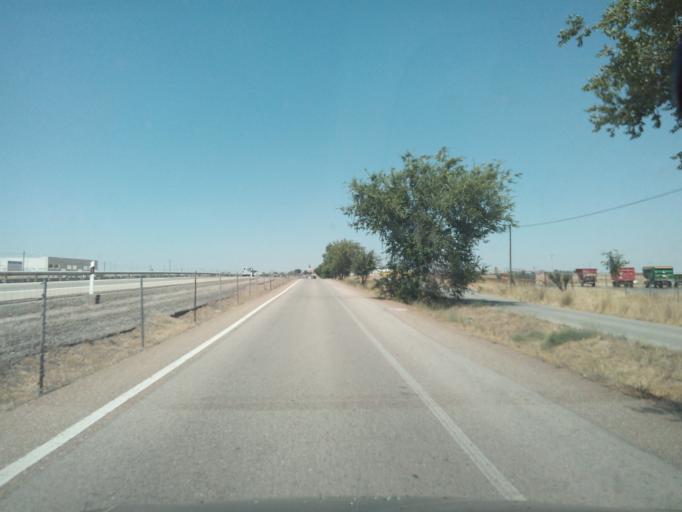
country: ES
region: Castille-La Mancha
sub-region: Province of Toledo
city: Tembleque
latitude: 39.7698
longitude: -3.4798
